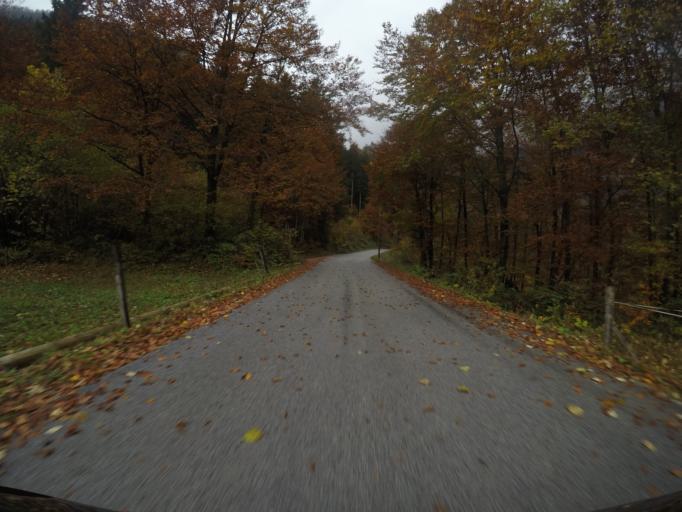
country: SI
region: Jesenice
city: Hrusica
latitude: 46.4015
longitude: 14.0013
